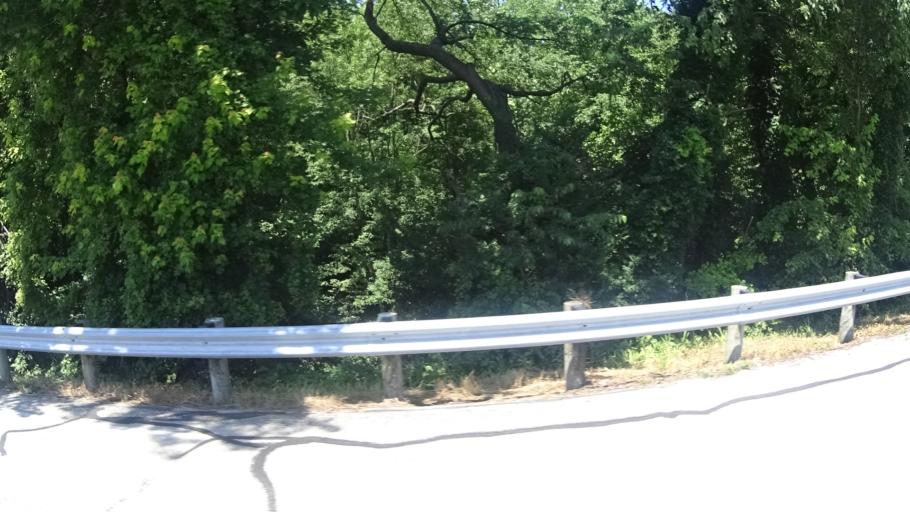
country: US
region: Ohio
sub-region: Huron County
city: Wakeman
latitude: 41.3447
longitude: -82.4330
